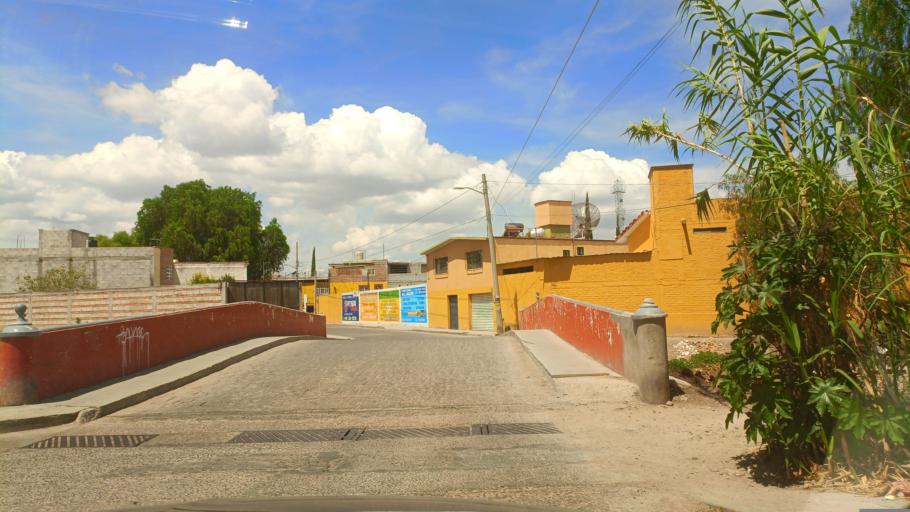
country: MX
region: Guanajuato
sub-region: San Luis de la Paz
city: San Luis de la Paz
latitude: 21.3038
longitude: -100.5169
